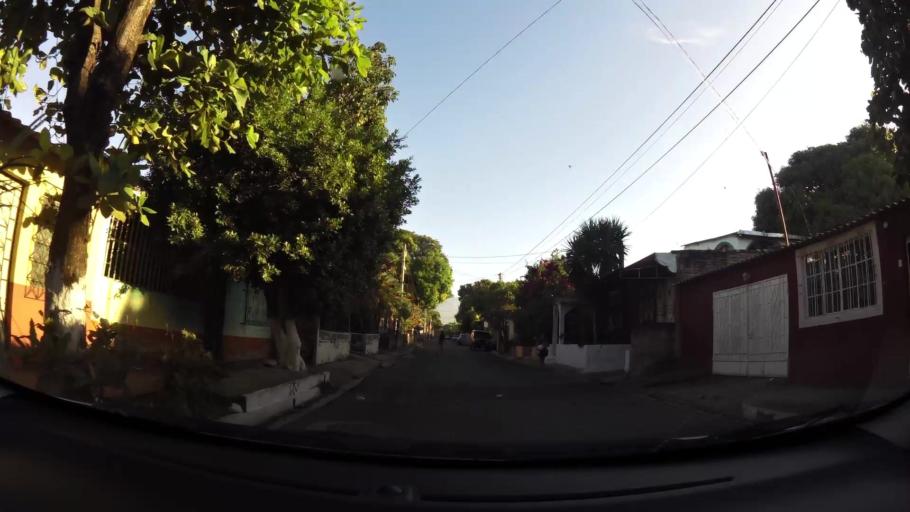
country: SV
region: Sonsonate
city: San Antonio del Monte
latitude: 13.7080
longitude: -89.7338
